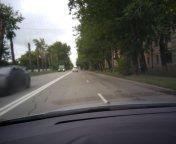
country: RU
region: Sverdlovsk
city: Sovkhoznyy
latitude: 56.7666
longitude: 60.6140
